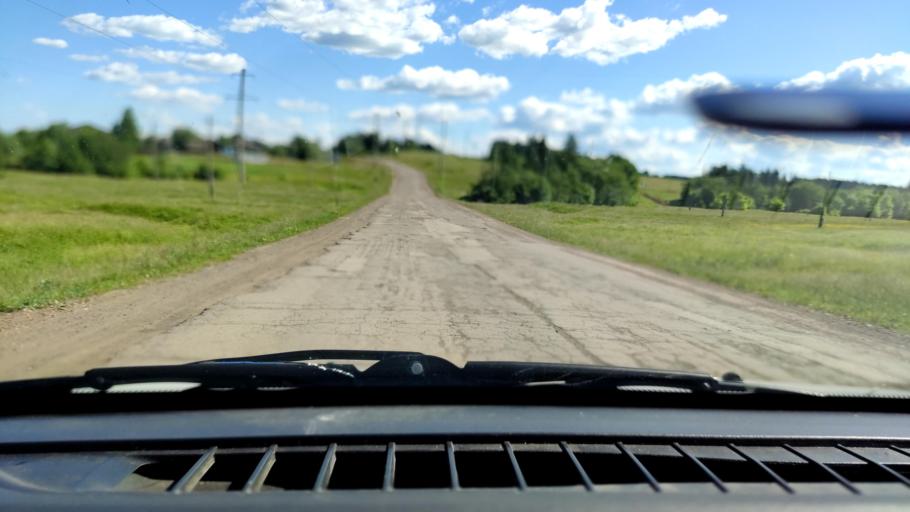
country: RU
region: Perm
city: Uinskoye
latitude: 57.1788
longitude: 56.5595
